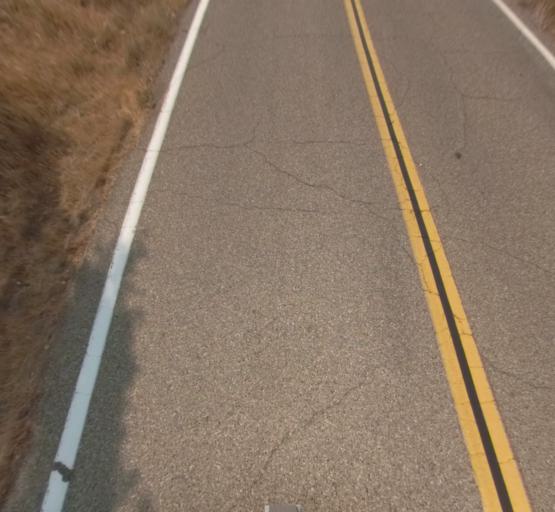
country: US
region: California
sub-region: Madera County
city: Yosemite Lakes
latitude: 37.2454
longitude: -119.8451
